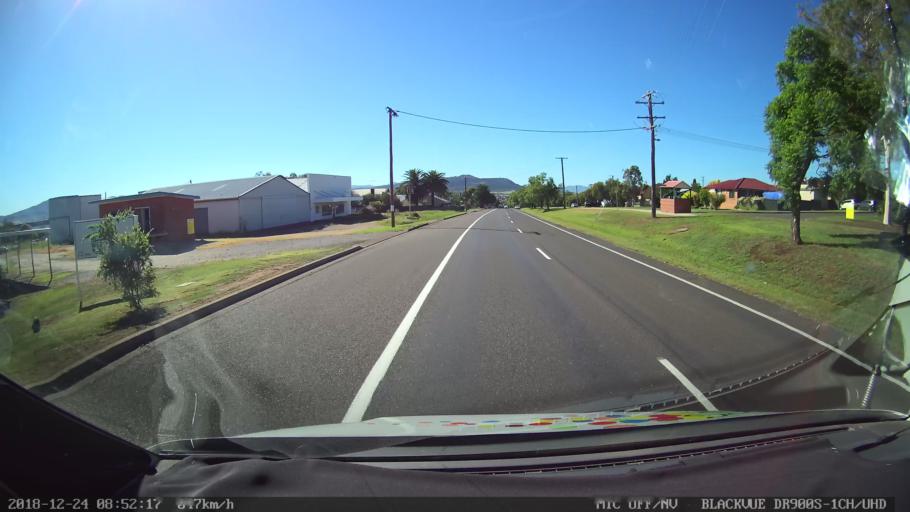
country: AU
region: New South Wales
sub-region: Liverpool Plains
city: Quirindi
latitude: -31.4906
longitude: 150.6785
